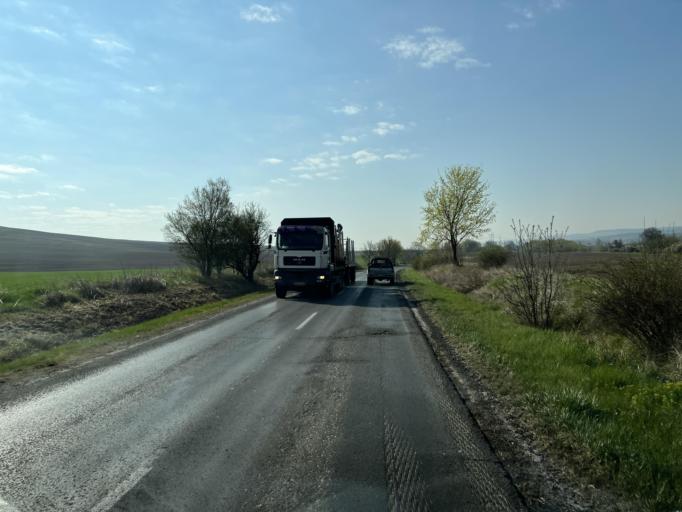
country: HU
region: Pest
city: Galgamacsa
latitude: 47.7225
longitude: 19.3796
